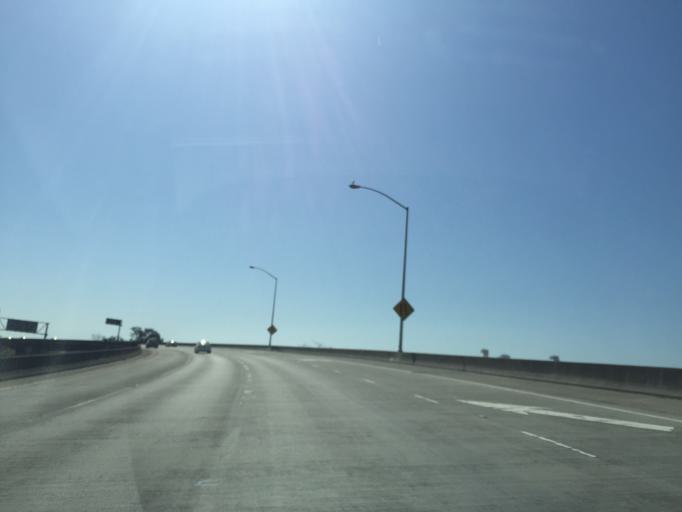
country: US
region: California
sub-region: Alameda County
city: Oakland
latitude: 37.8023
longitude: -122.2804
